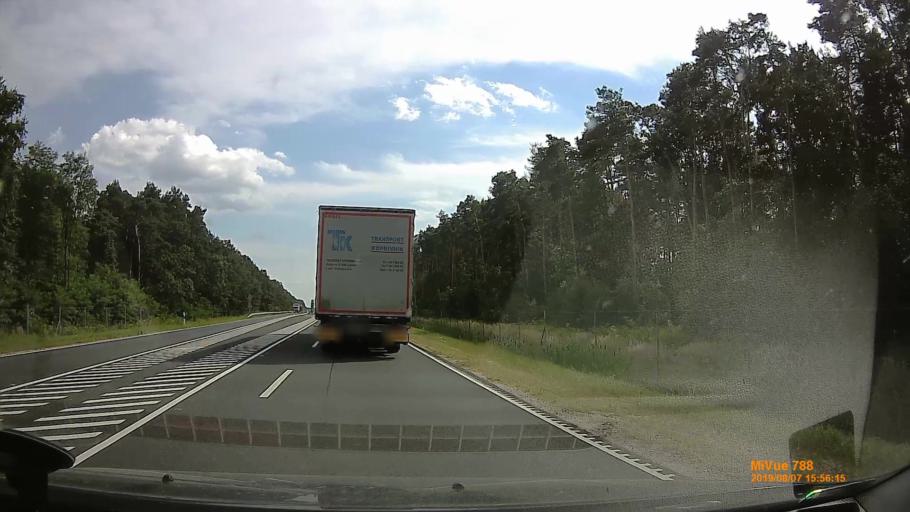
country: HU
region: Vas
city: Kormend
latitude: 47.0633
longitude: 16.6164
